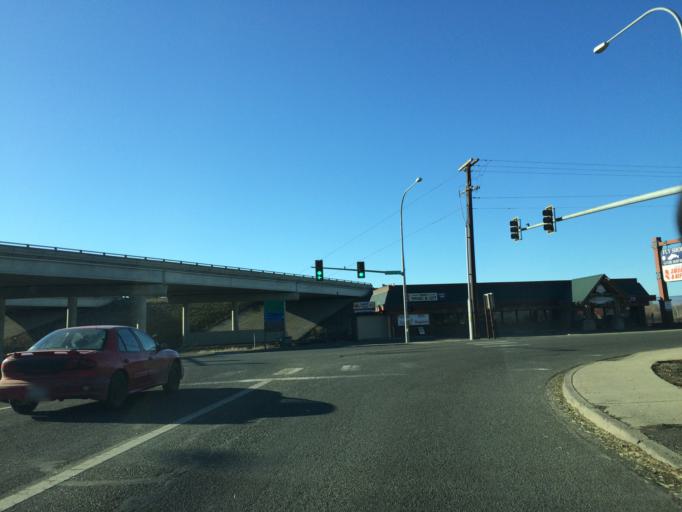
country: US
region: Washington
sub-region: Kittitas County
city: Ellensburg
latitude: 46.9744
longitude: -120.5407
